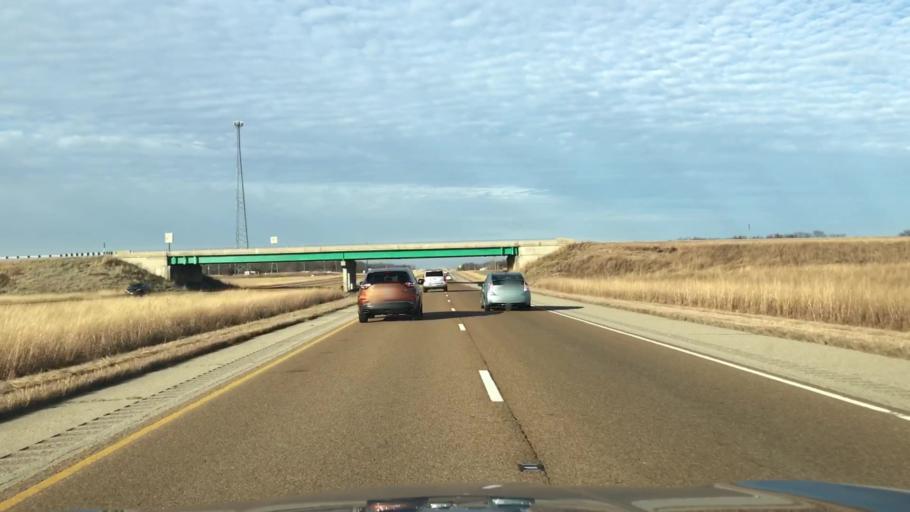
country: US
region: Illinois
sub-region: Montgomery County
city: Raymond
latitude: 39.2768
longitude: -89.6417
